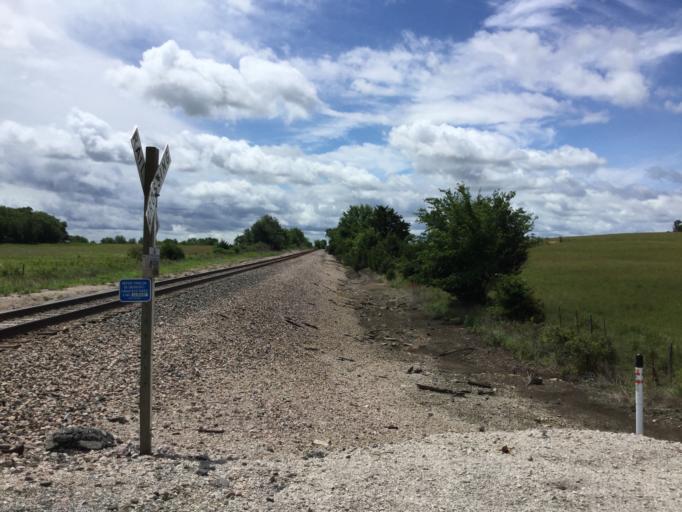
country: US
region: Kansas
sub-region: Crawford County
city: Arma
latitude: 37.6886
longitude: -94.7991
